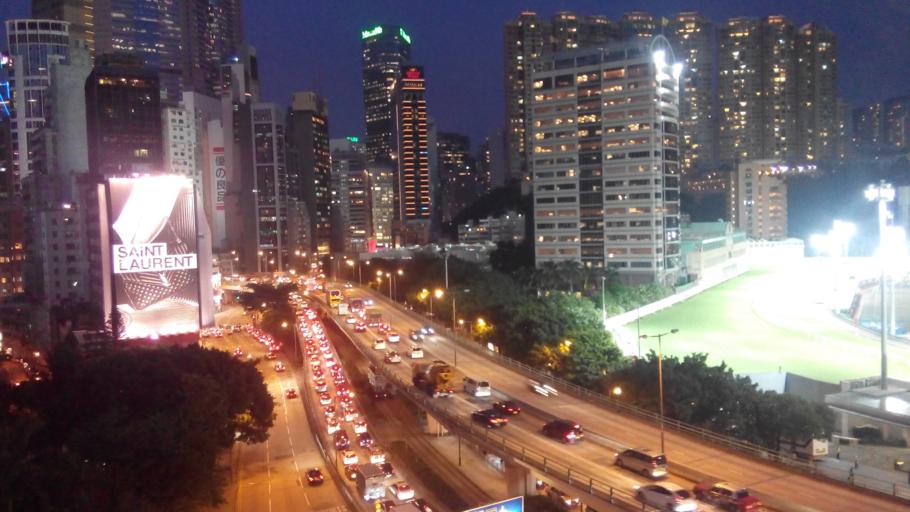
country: HK
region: Wanchai
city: Wan Chai
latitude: 22.2756
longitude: 114.1810
